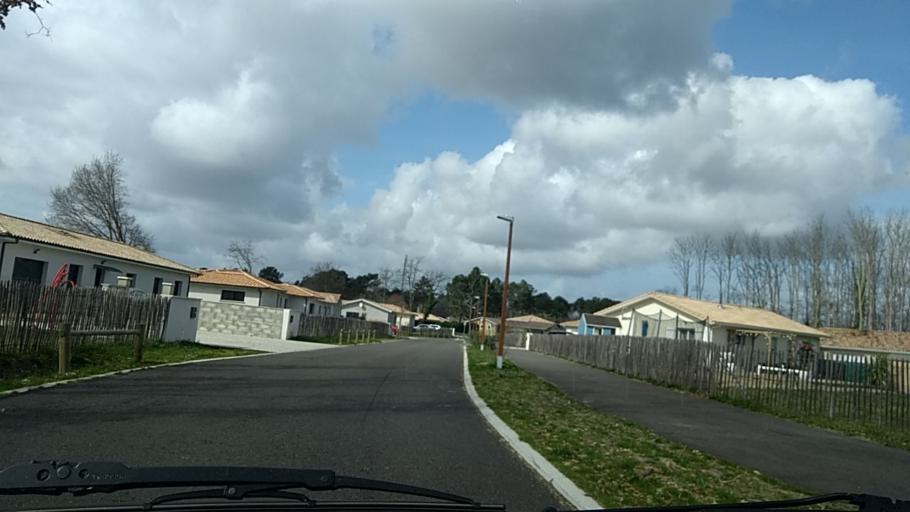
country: FR
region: Aquitaine
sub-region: Departement de la Gironde
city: Salles
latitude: 44.5462
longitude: -0.8764
